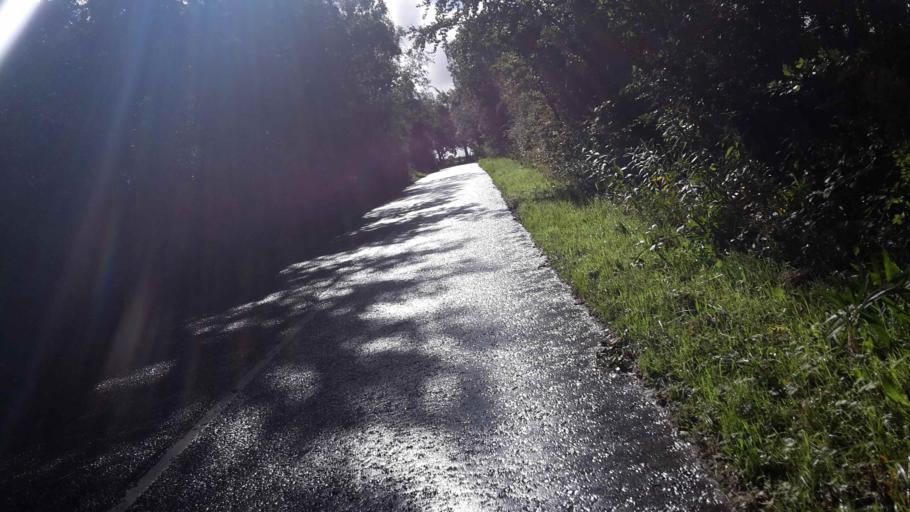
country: GB
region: Scotland
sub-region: South Lanarkshire
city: Carluke
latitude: 55.7258
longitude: -3.8544
